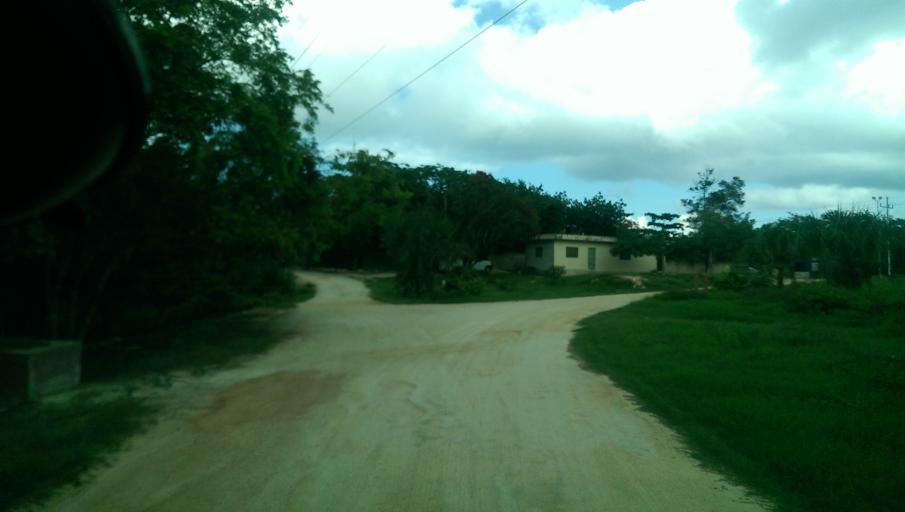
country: MX
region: Quintana Roo
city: Playa del Carmen
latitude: 20.5882
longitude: -87.1348
